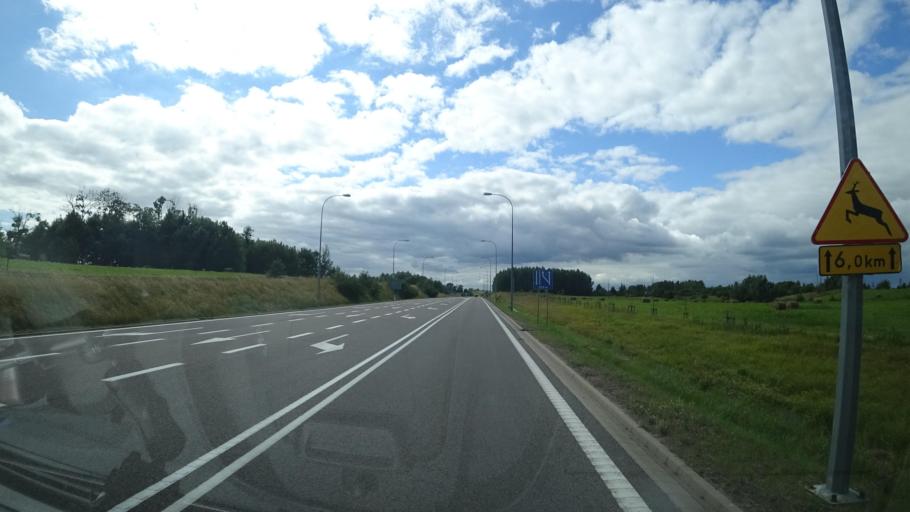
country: PL
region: Warmian-Masurian Voivodeship
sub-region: Powiat goldapski
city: Goldap
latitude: 54.2979
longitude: 22.2953
